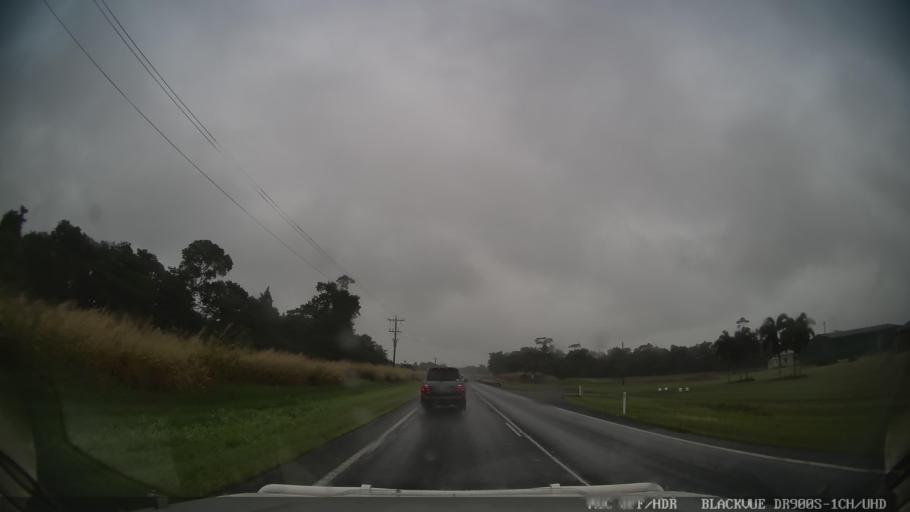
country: AU
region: Queensland
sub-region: Cassowary Coast
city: Innisfail
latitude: -17.6555
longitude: 146.0358
